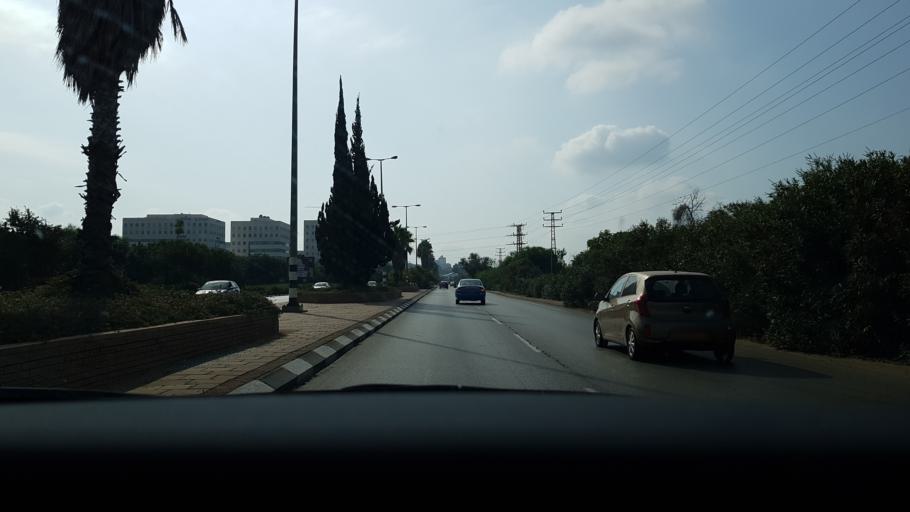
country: IL
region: Central District
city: Ness Ziona
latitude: 31.9175
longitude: 34.7997
